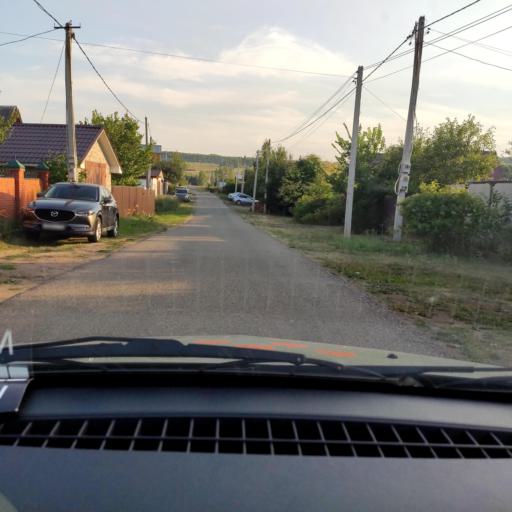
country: RU
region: Bashkortostan
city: Avdon
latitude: 54.5835
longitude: 55.6698
